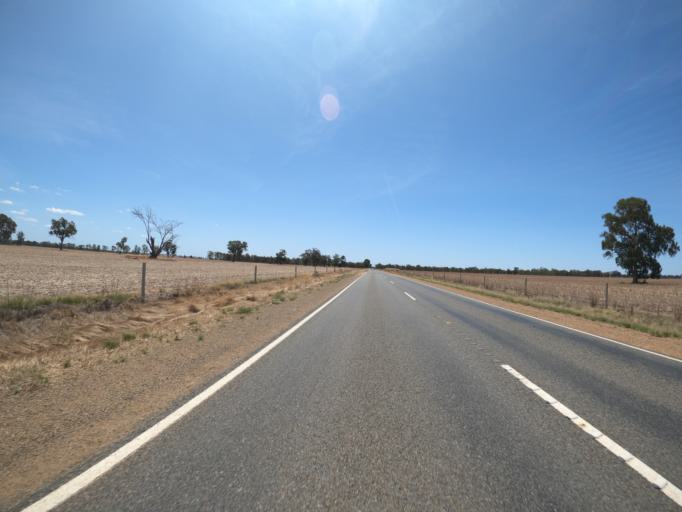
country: AU
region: Victoria
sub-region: Moira
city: Yarrawonga
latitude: -36.1680
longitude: 145.9672
